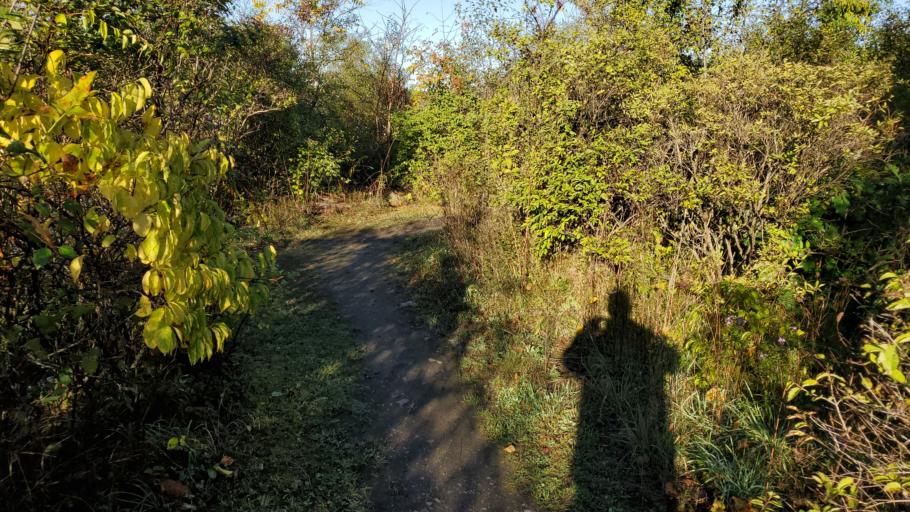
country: CA
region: Ontario
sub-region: Lanark County
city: Smiths Falls
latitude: 44.9172
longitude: -75.8423
